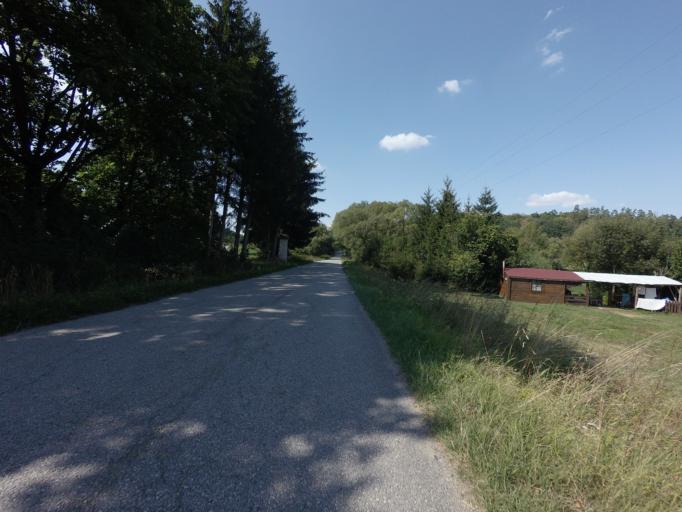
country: CZ
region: Jihocesky
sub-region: Okres Ceske Budejovice
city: Hluboka nad Vltavou
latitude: 49.1346
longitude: 14.4495
